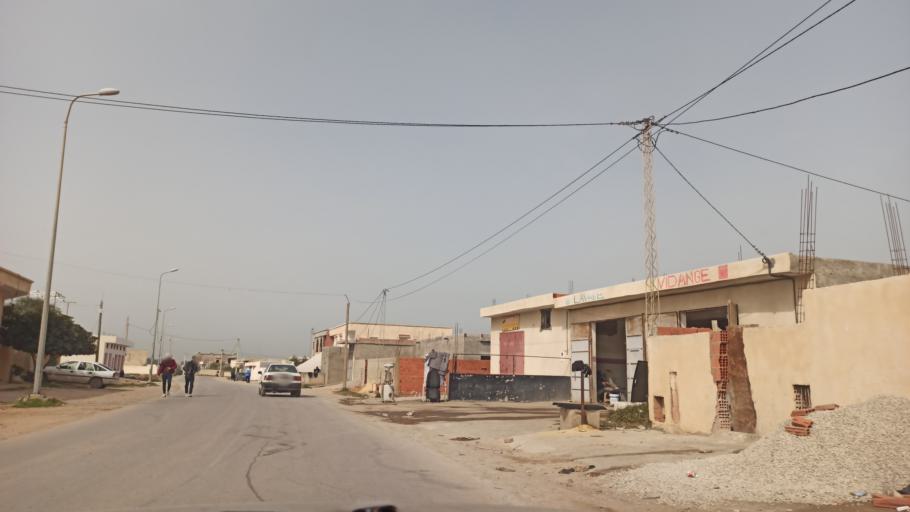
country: TN
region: Zaghwan
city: Zaghouan
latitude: 36.4170
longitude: 10.1222
